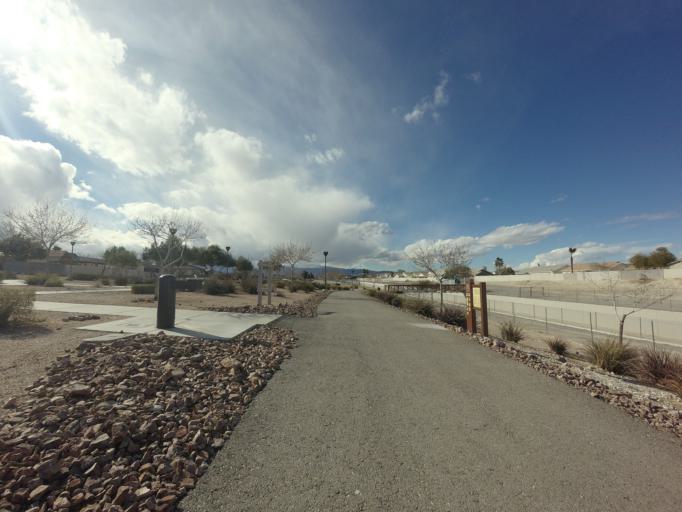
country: US
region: Nevada
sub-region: Clark County
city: North Las Vegas
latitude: 36.2574
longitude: -115.1744
